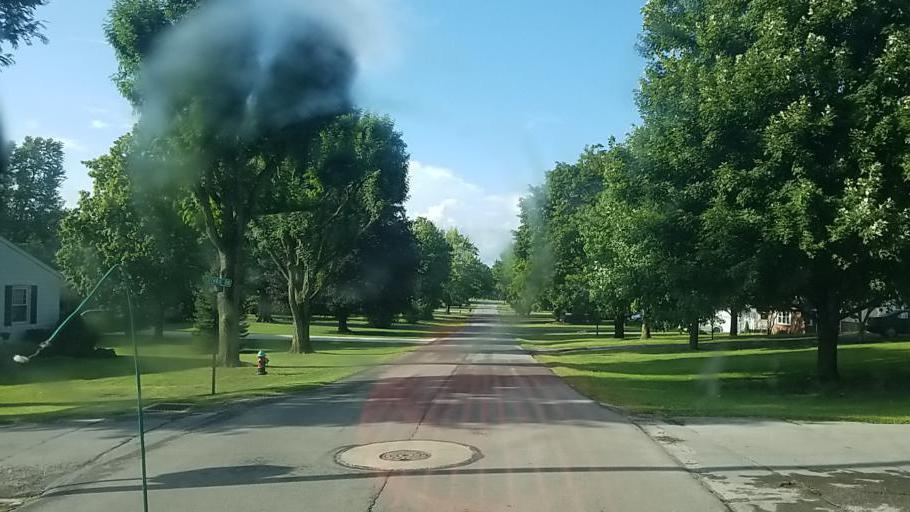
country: US
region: Ohio
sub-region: Wyandot County
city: Upper Sandusky
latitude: 40.8329
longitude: -83.2782
